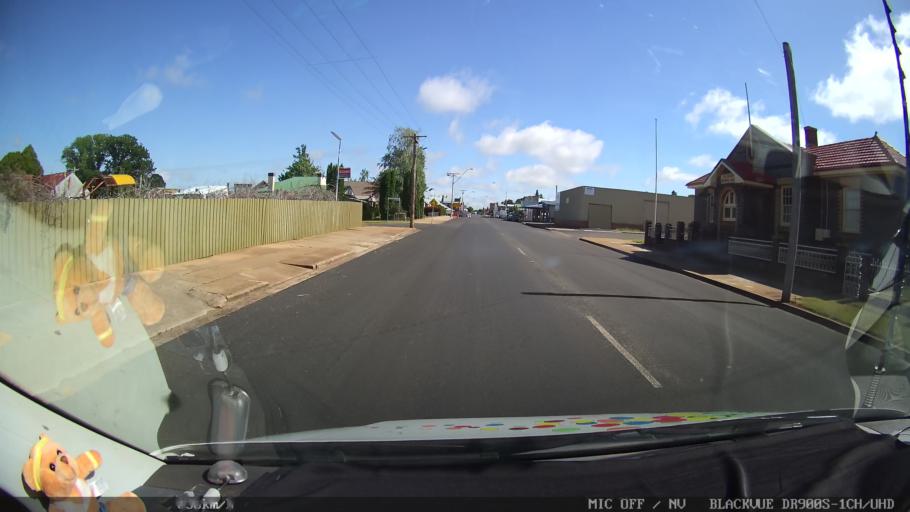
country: AU
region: New South Wales
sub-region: Guyra
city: Guyra
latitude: -30.2221
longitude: 151.6713
